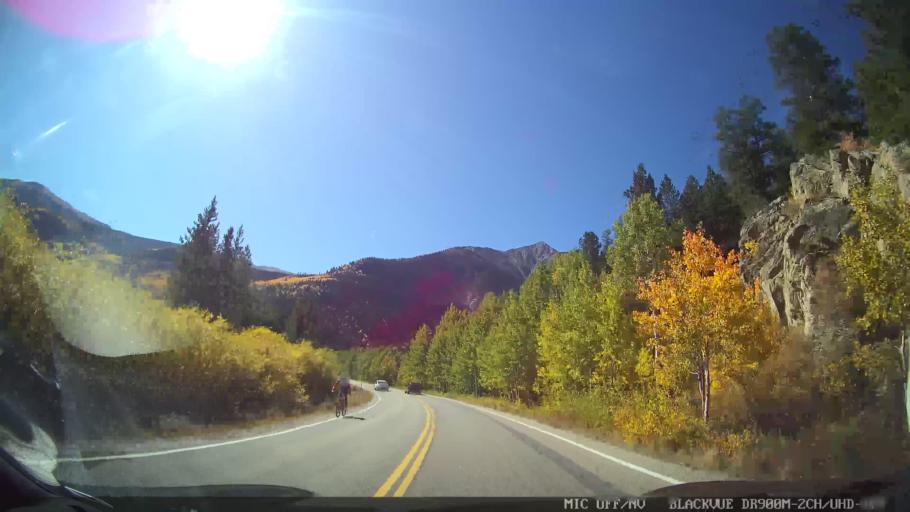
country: US
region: Colorado
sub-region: Lake County
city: Leadville
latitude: 39.0702
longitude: -106.4011
